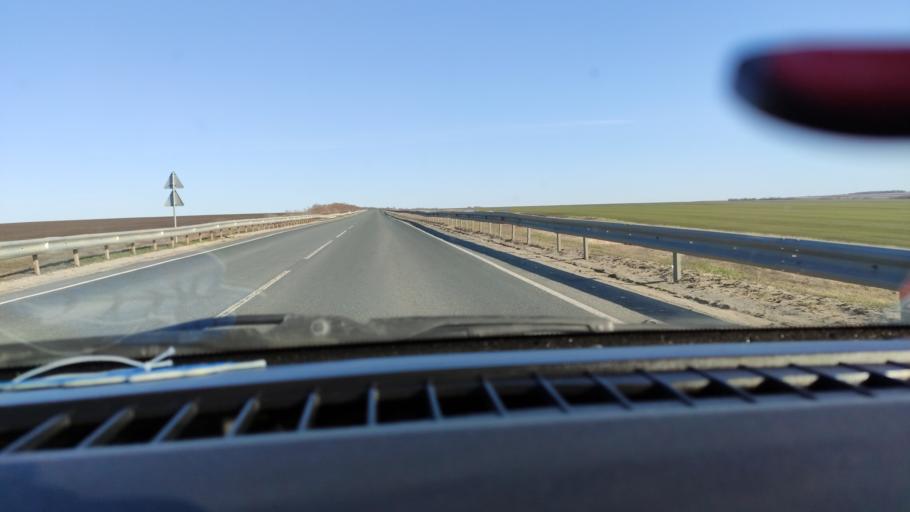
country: RU
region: Saratov
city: Dukhovnitskoye
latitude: 52.7538
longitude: 48.2459
